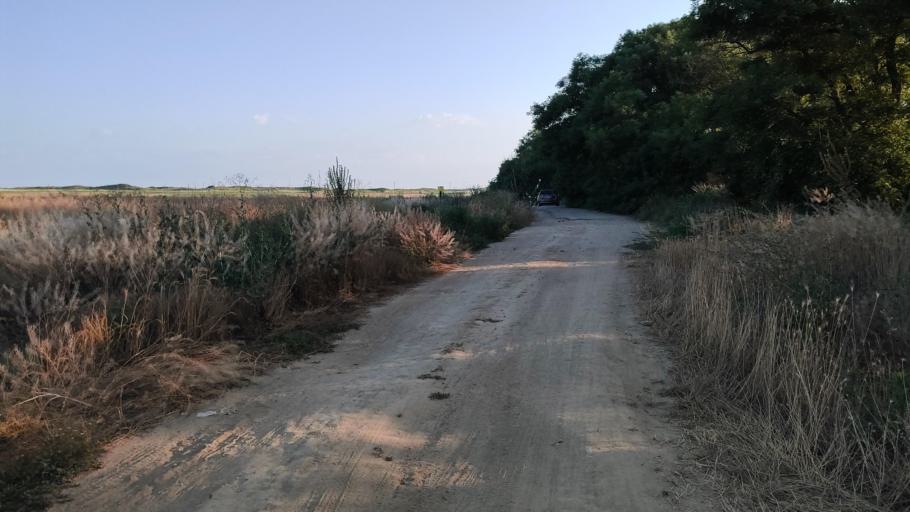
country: RU
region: Krasnodarskiy
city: Blagovetschenskaya
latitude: 45.0687
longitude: 37.0558
